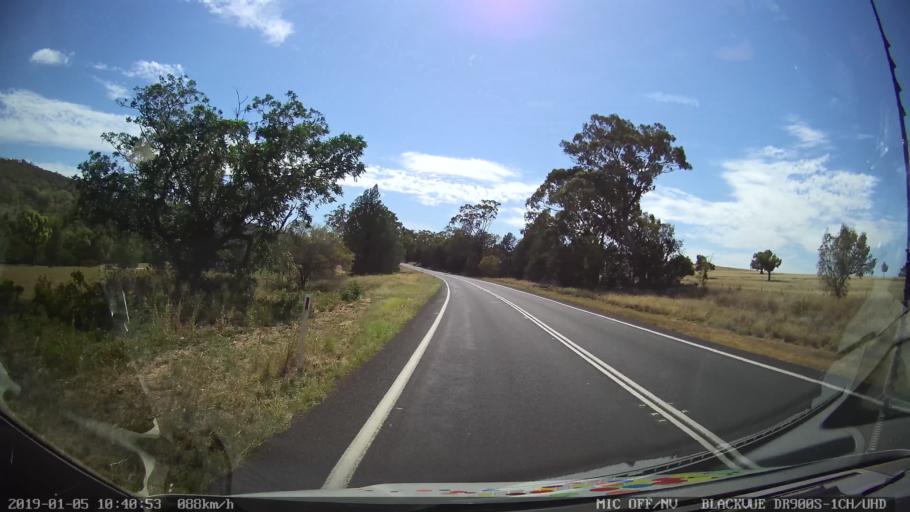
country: AU
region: New South Wales
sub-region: Warrumbungle Shire
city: Coonabarabran
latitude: -31.4663
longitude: 148.9511
